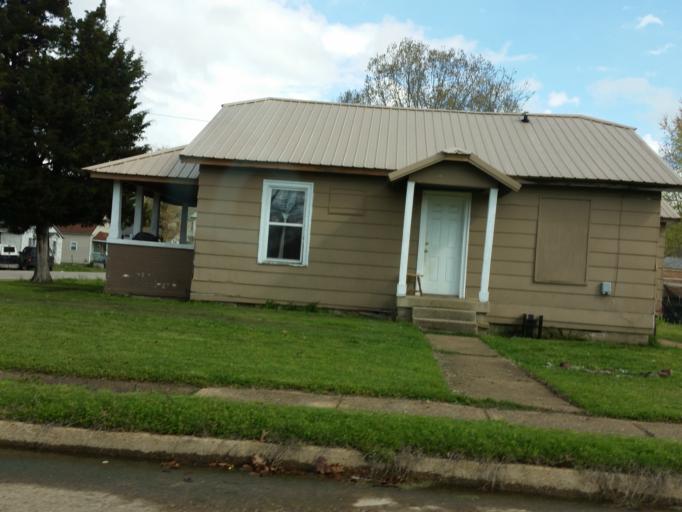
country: US
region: Missouri
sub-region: Butler County
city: Poplar Bluff
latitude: 36.7623
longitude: -90.3902
